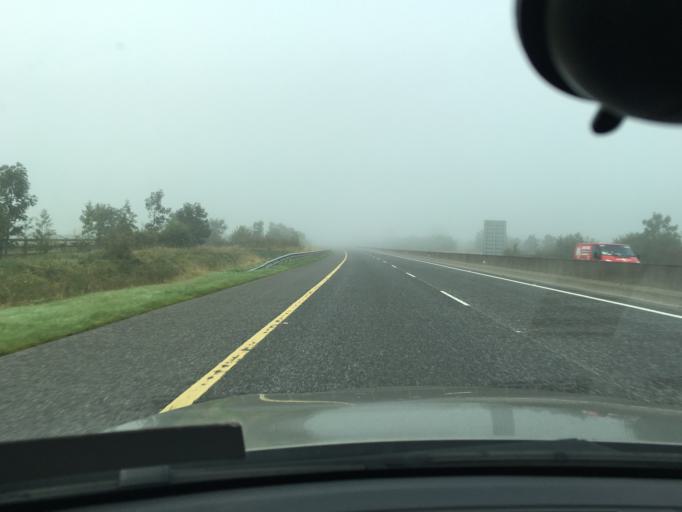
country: IE
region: Leinster
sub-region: An Iarmhi
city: Kinnegad
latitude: 53.4501
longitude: -7.1498
